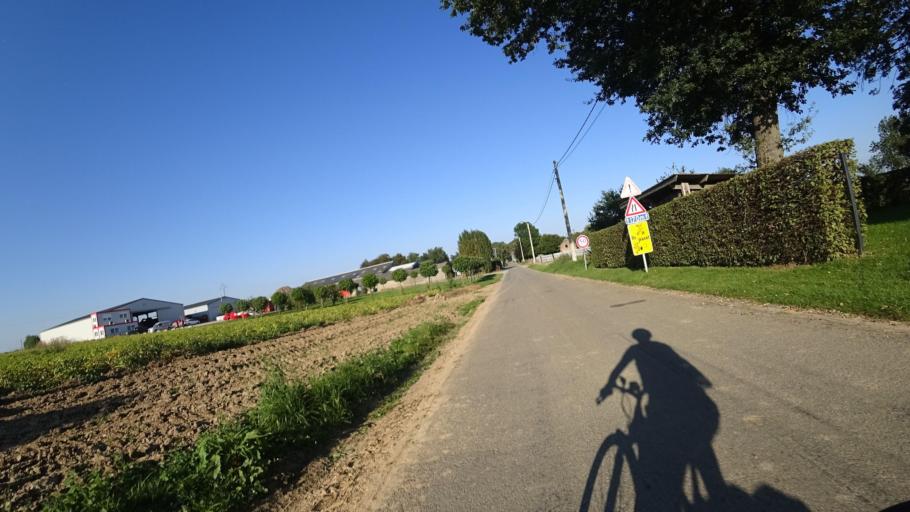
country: BE
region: Wallonia
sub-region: Province de Namur
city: Namur
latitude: 50.5414
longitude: 4.8337
